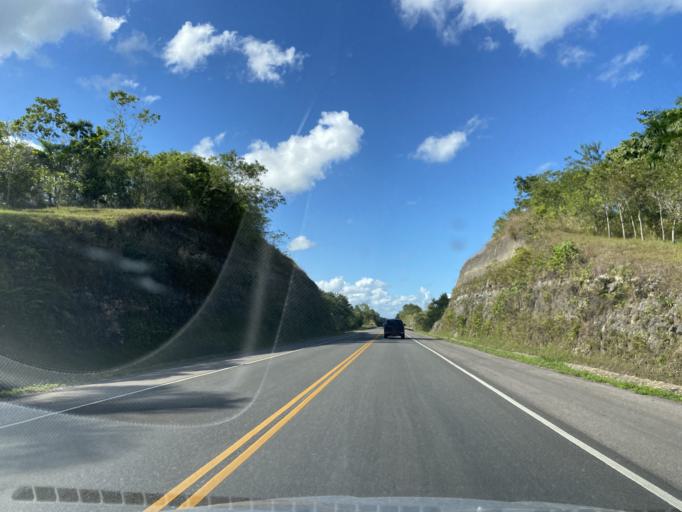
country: DO
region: Monte Plata
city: Gonzalo
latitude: 18.9678
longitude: -69.7742
